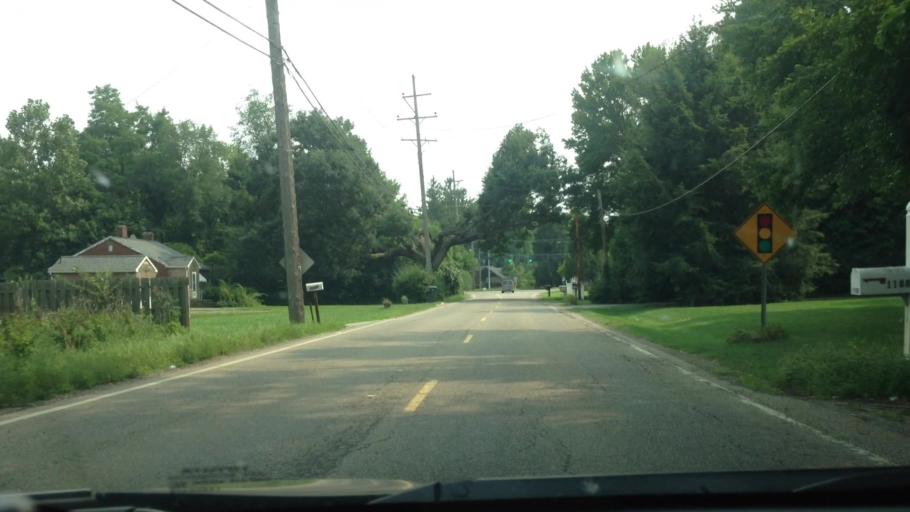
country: US
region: Ohio
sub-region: Summit County
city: Fairlawn
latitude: 41.0850
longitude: -81.5904
